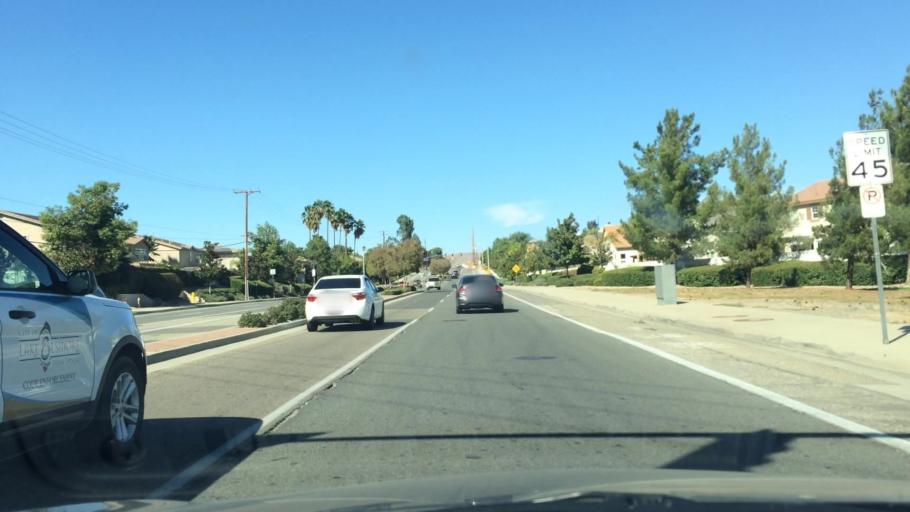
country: US
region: California
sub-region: Riverside County
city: Lake Elsinore
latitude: 33.6949
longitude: -117.3900
